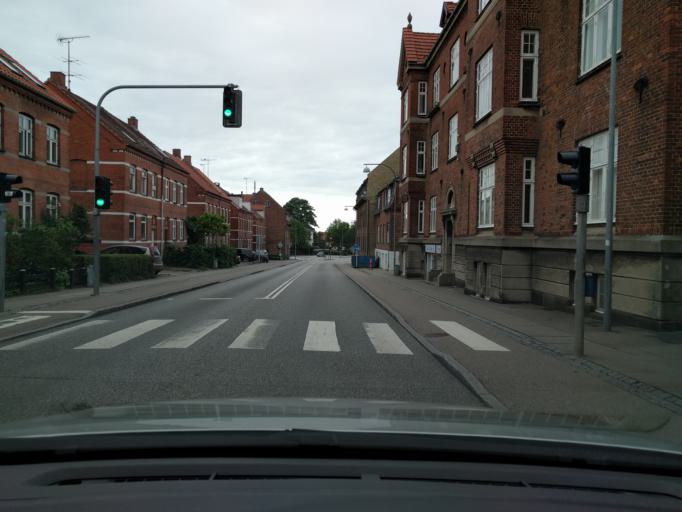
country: DK
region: Zealand
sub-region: Roskilde Kommune
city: Roskilde
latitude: 55.6392
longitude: 12.0737
